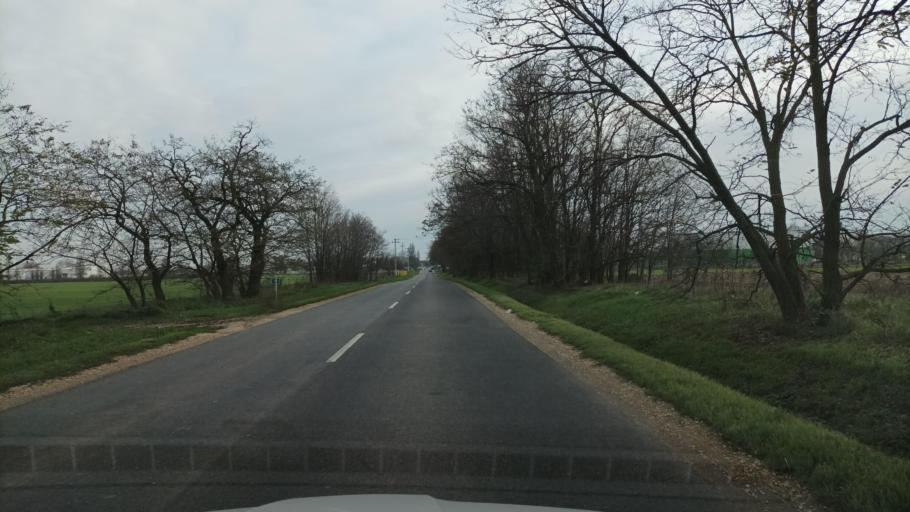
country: HU
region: Pest
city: Ocsa
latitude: 47.3095
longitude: 19.2105
